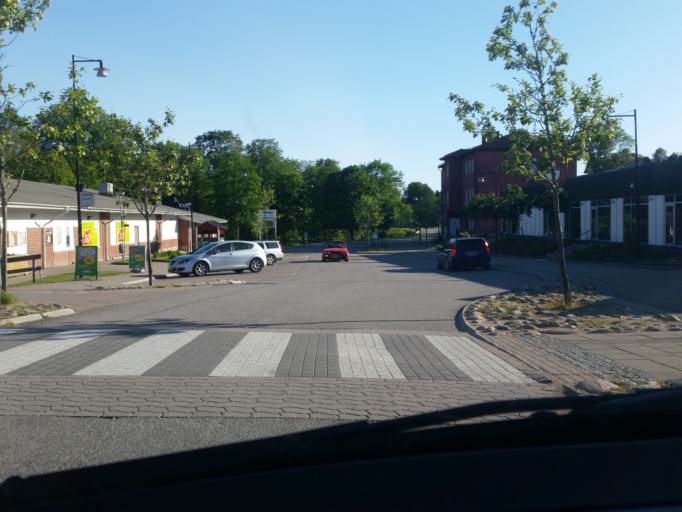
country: SE
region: Vaestra Goetaland
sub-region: Fargelanda Kommun
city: Faergelanda
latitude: 58.5677
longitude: 11.9965
